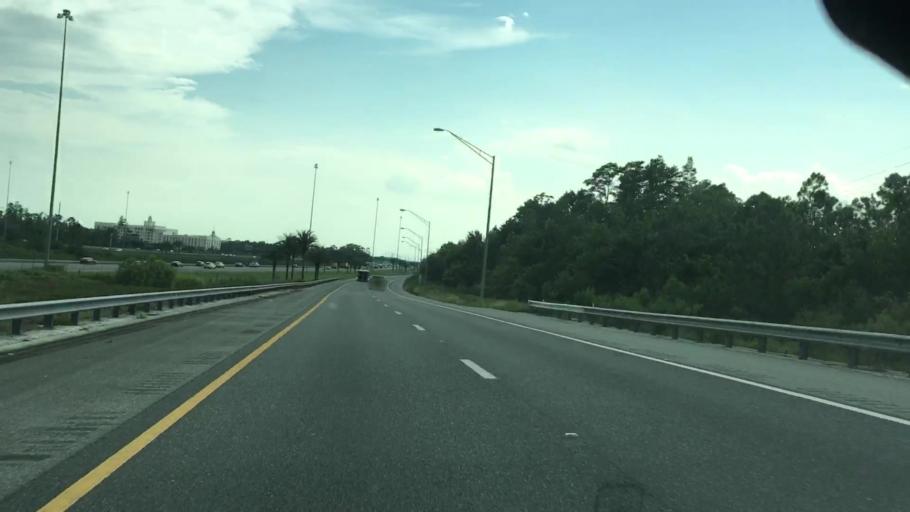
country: US
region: Florida
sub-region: Osceola County
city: Celebration
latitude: 28.3248
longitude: -81.5543
